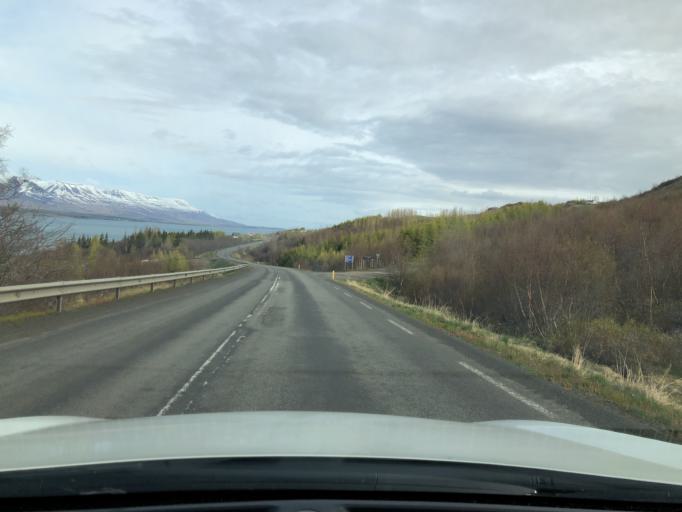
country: IS
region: Northeast
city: Akureyri
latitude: 65.6989
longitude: -18.0589
